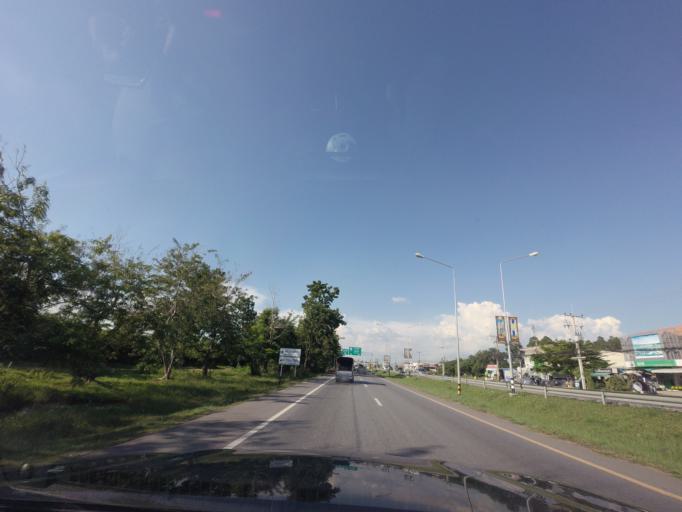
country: TH
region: Khon Kaen
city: Non Sila
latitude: 15.9633
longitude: 102.6904
